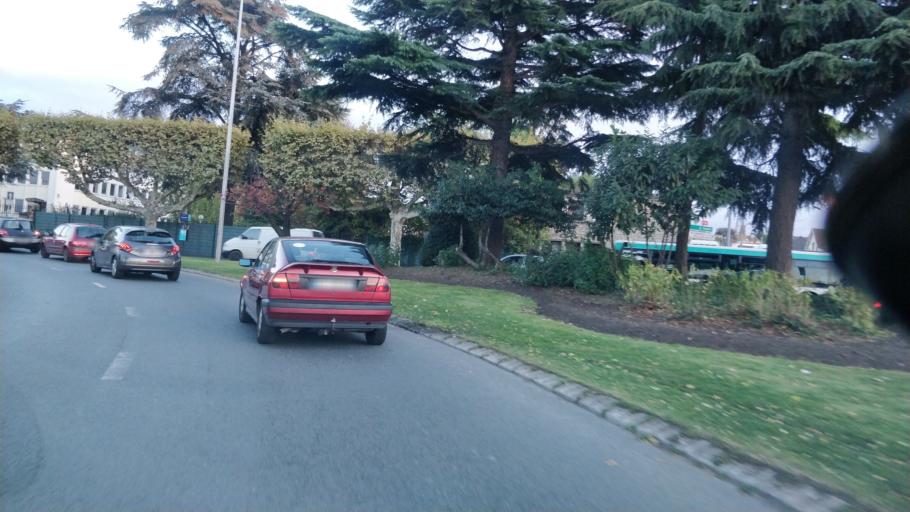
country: FR
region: Ile-de-France
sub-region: Departement de Seine-Saint-Denis
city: Villemomble
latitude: 48.8815
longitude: 2.4950
